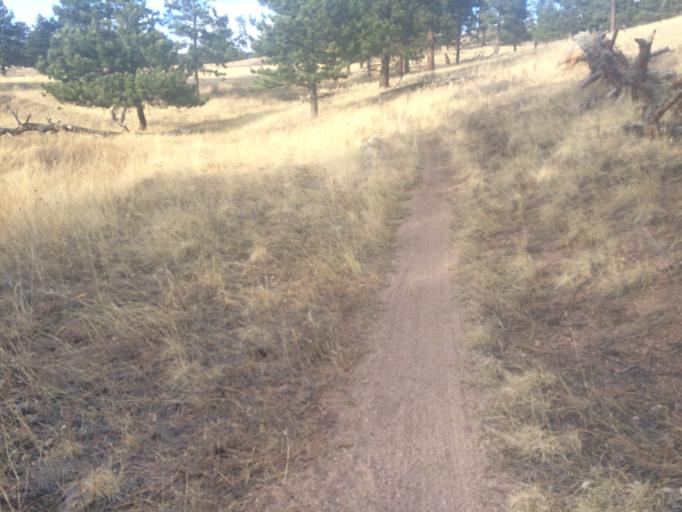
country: US
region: Colorado
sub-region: Boulder County
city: Coal Creek
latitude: 39.9569
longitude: -105.3408
